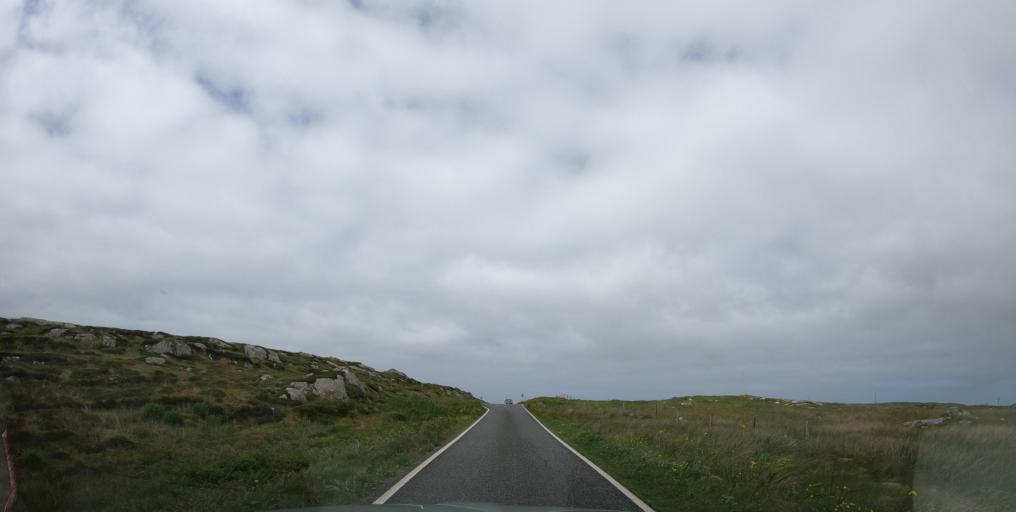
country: GB
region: Scotland
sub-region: Eilean Siar
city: Isle of South Uist
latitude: 57.1032
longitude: -7.3519
